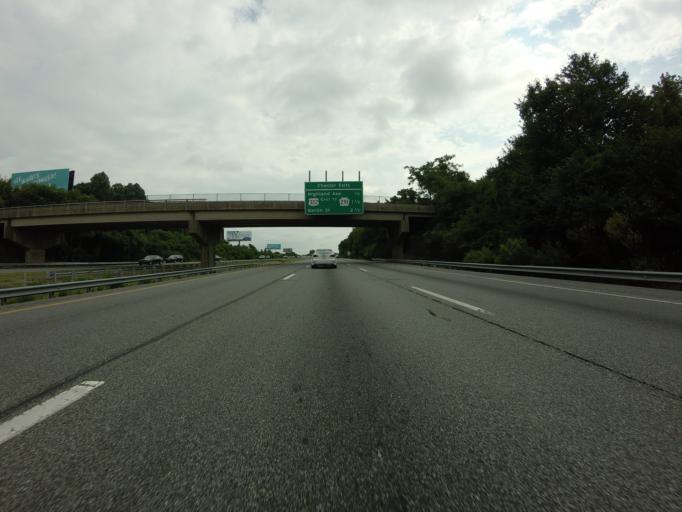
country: US
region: Pennsylvania
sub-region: Delaware County
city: Trainer
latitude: 39.8363
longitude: -75.4176
